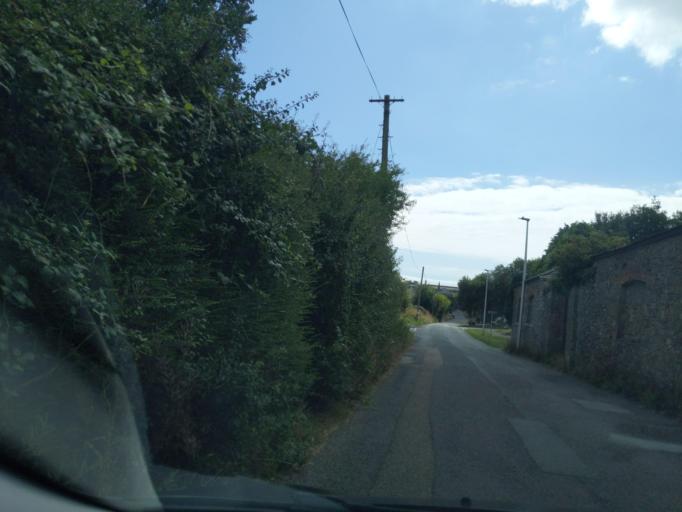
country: GB
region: England
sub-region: Devon
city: Modbury
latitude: 50.3536
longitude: -3.8881
